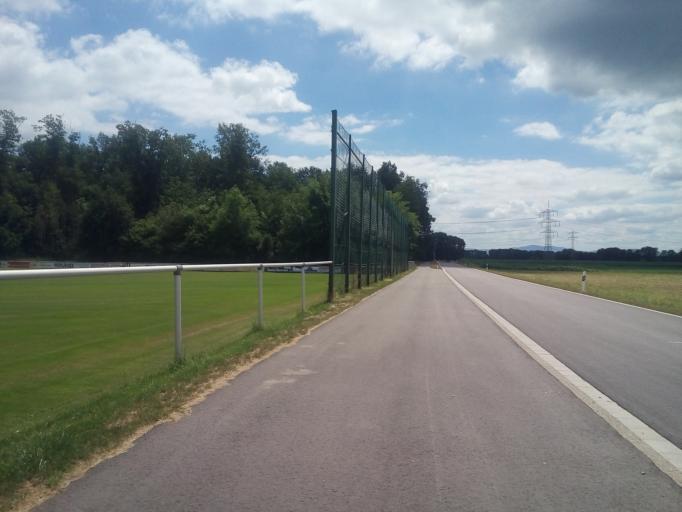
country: DE
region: Baden-Wuerttemberg
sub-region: Freiburg Region
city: Rheinau
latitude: 48.6487
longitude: 7.9362
